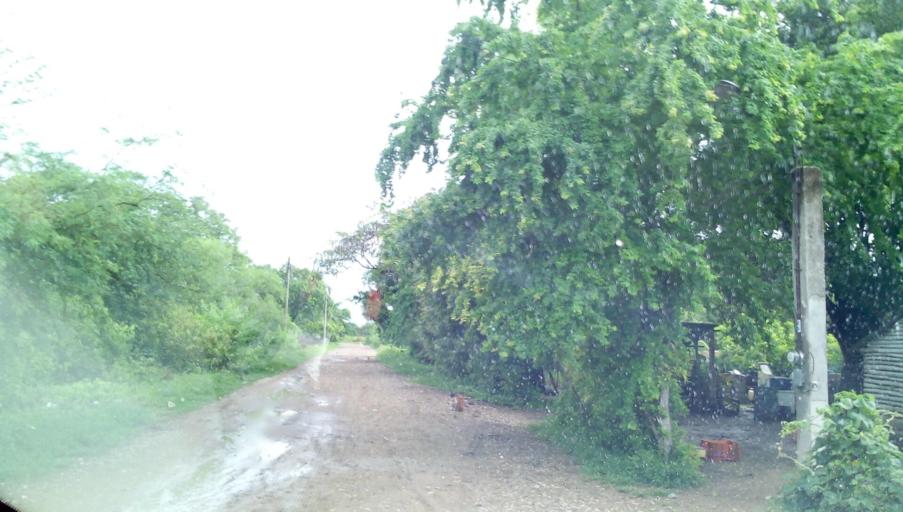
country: MX
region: Veracruz
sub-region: Panuco
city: Guayalejo
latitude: 22.3239
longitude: -98.3351
